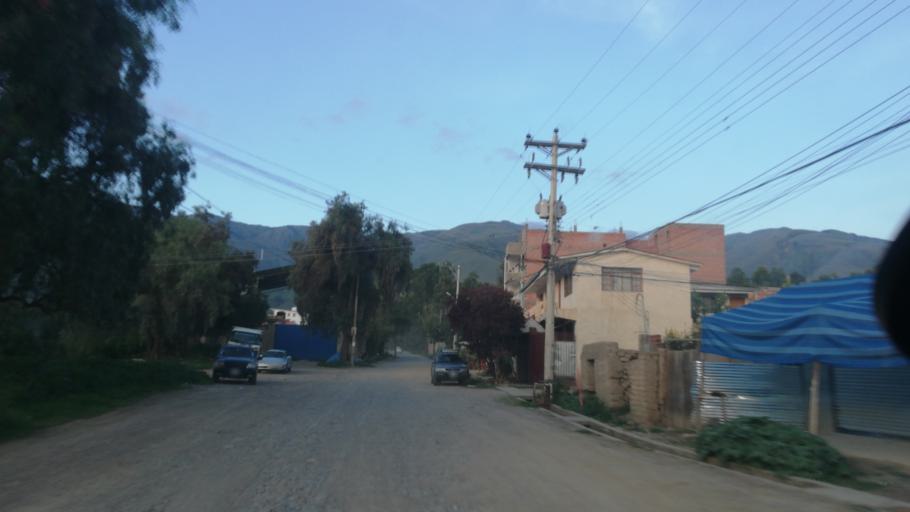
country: BO
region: Cochabamba
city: Cochabamba
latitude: -17.3459
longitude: -66.2122
